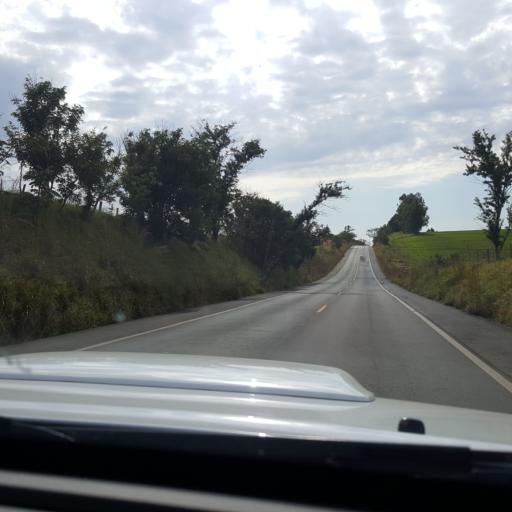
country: BR
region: Sao Paulo
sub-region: Itaporanga
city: Itaporanga
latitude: -23.7537
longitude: -49.4519
